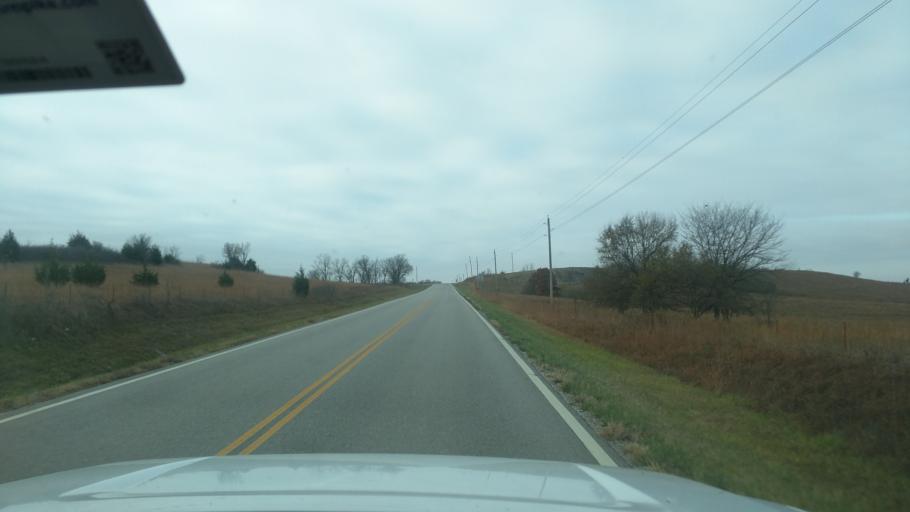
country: US
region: Kansas
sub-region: Greenwood County
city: Eureka
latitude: 37.6954
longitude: -96.2254
